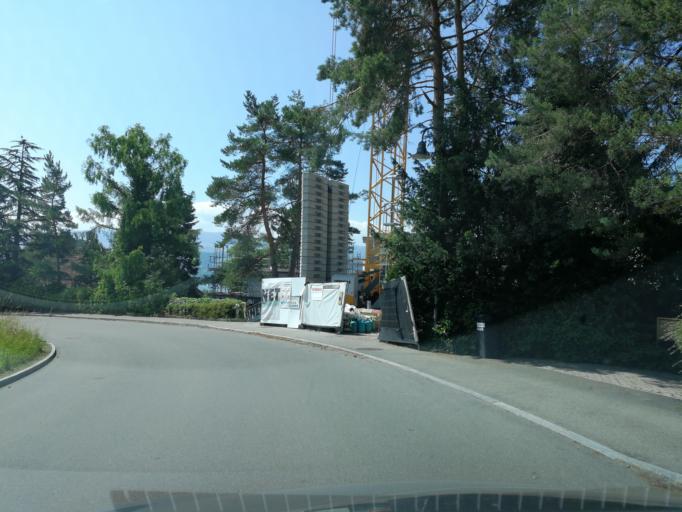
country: CH
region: Zurich
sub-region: Bezirk Meilen
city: Meilen
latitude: 47.2767
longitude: 8.6422
